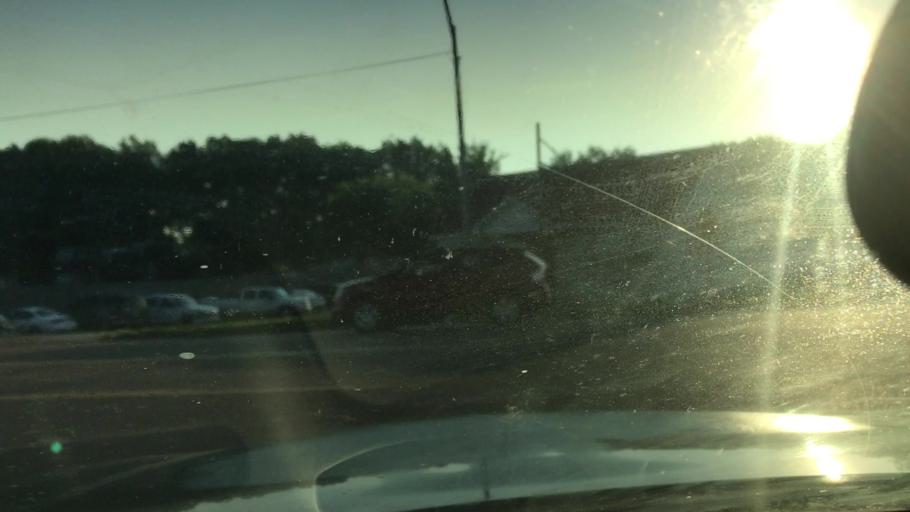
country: US
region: Mississippi
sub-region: De Soto County
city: Southaven
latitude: 35.0715
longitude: -89.9466
